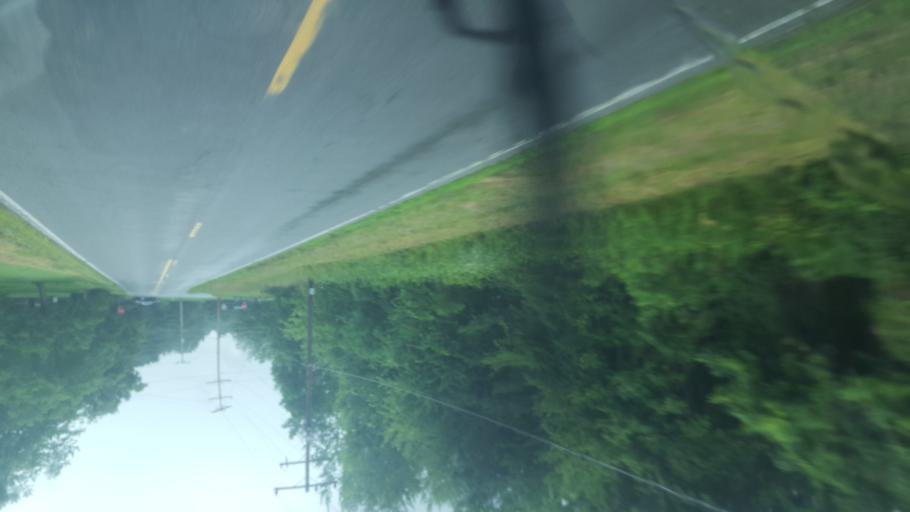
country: US
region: Ohio
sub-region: Delaware County
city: Sunbury
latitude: 40.2466
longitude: -82.9090
